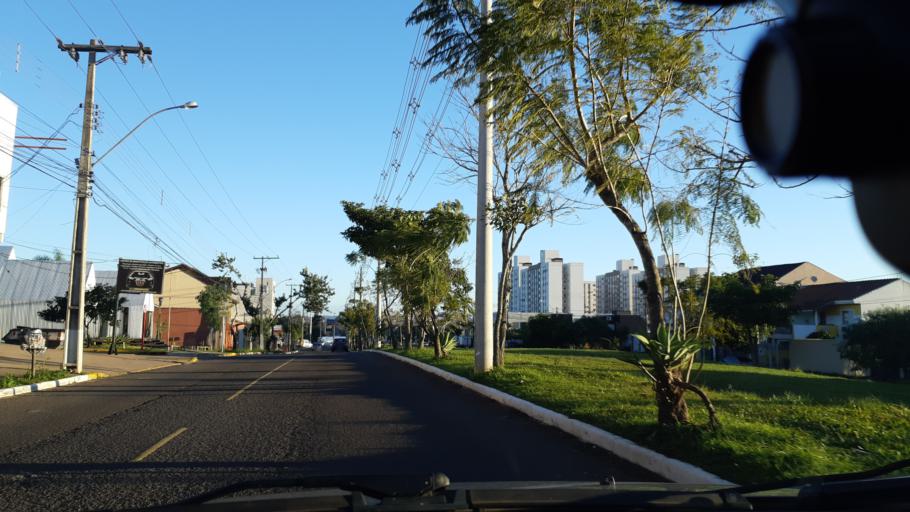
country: BR
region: Rio Grande do Sul
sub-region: Canoas
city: Canoas
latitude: -29.9160
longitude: -51.1544
